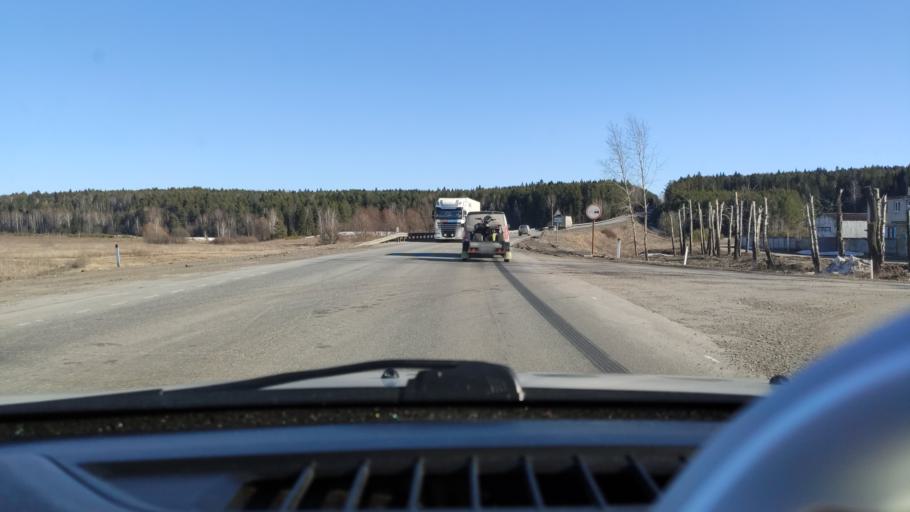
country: RU
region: Perm
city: Kungur
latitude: 57.4515
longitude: 56.8063
